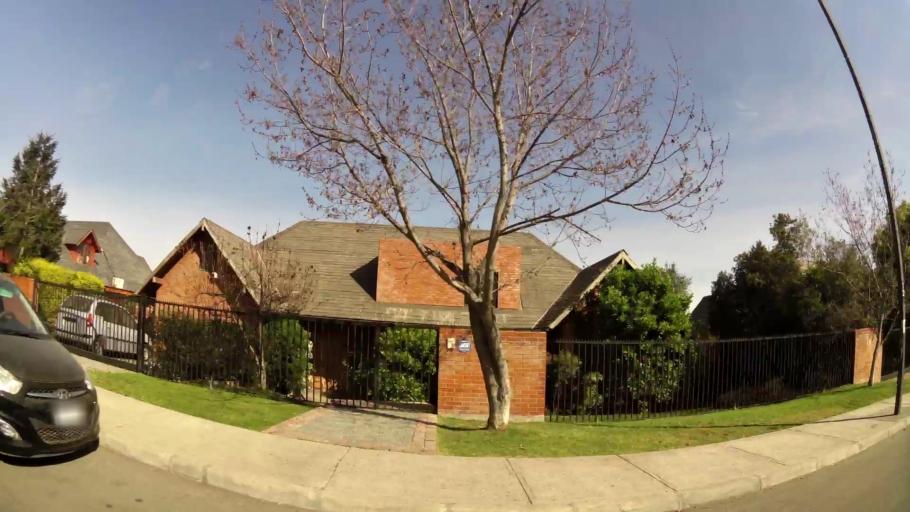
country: CL
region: Santiago Metropolitan
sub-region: Provincia de Santiago
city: Villa Presidente Frei, Nunoa, Santiago, Chile
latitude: -33.4996
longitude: -70.5269
